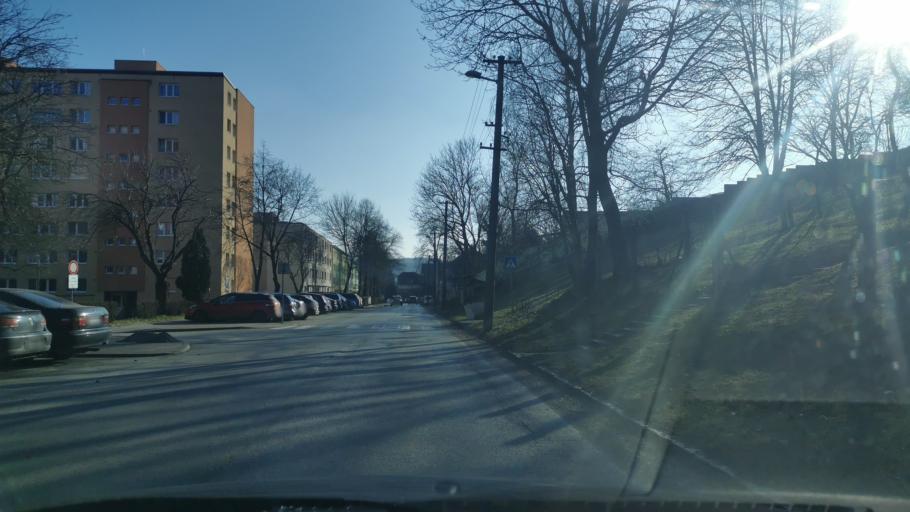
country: SK
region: Trenciansky
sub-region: Okres Myjava
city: Myjava
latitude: 48.7500
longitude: 17.5634
